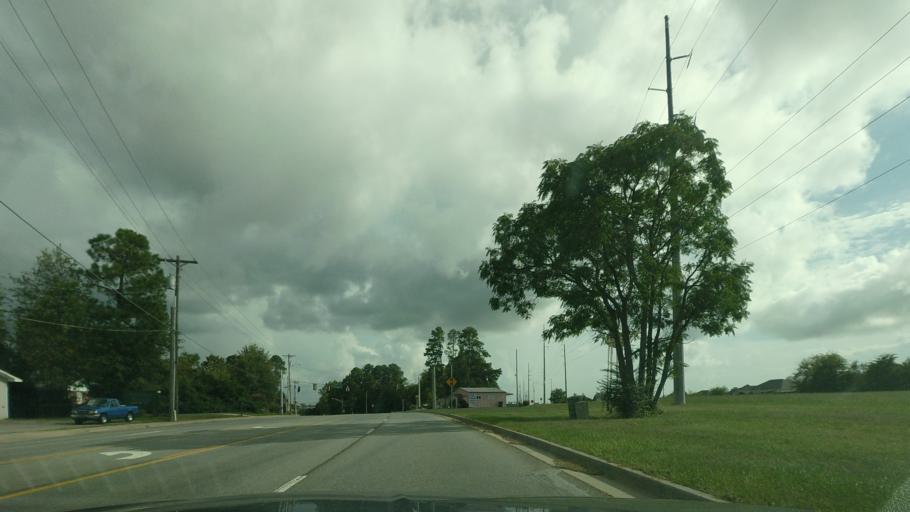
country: US
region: Georgia
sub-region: Houston County
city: Centerville
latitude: 32.6275
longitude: -83.6897
